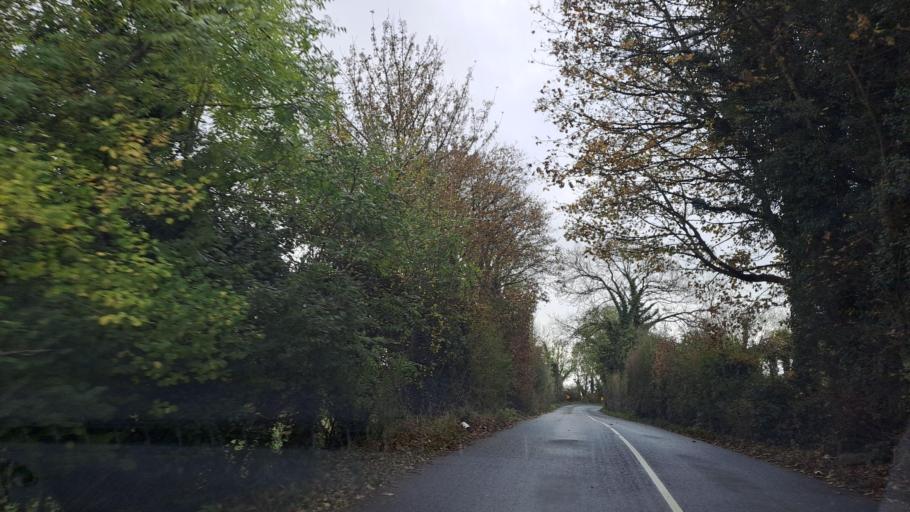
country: IE
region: Ulster
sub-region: An Cabhan
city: Virginia
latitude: 53.8562
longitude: -7.0464
